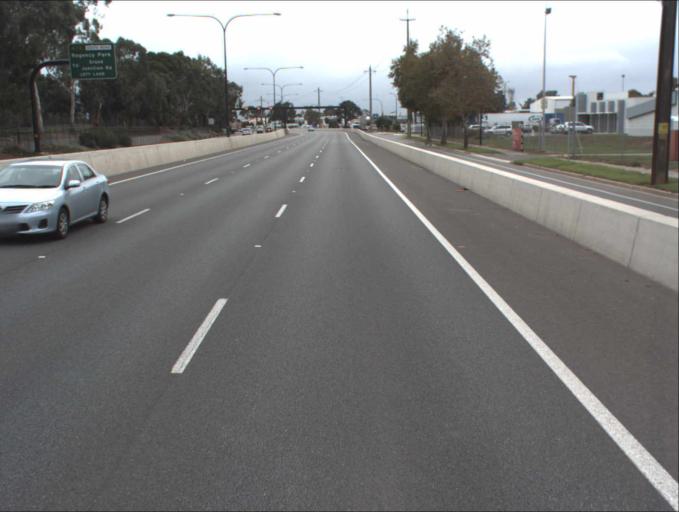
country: AU
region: South Australia
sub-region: Charles Sturt
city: Woodville
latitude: -34.8678
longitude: 138.5707
